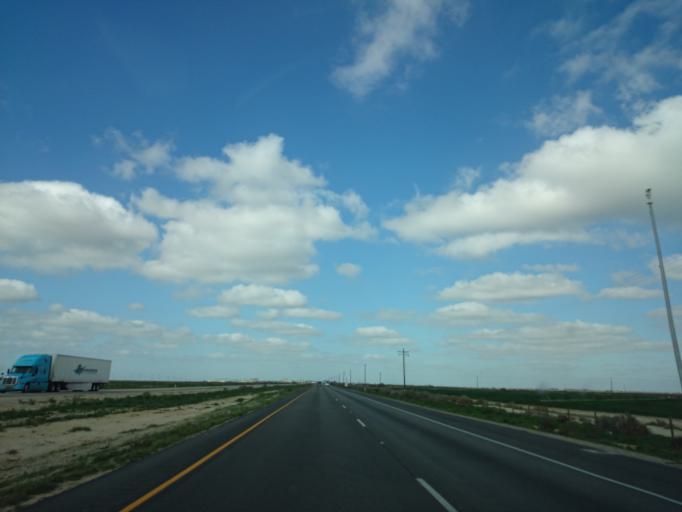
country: US
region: California
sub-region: Kern County
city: Rosedale
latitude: 35.2712
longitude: -119.2288
